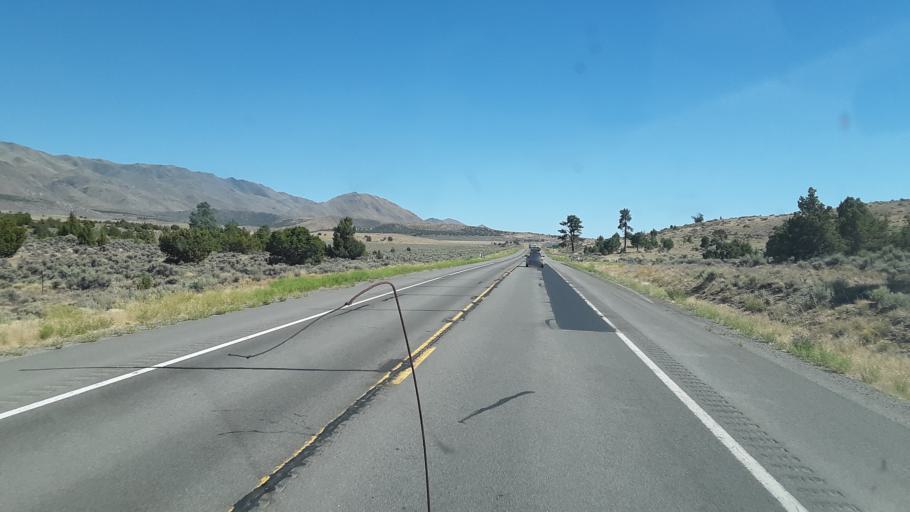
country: US
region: Nevada
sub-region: Washoe County
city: Cold Springs
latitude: 39.8315
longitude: -120.0380
